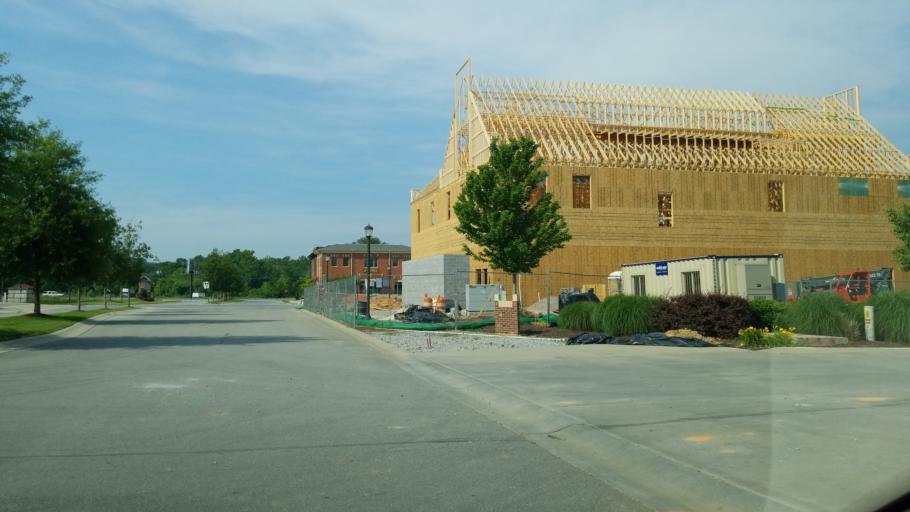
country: US
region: Tennessee
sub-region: Hamilton County
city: Collegedale
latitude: 35.0832
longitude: -85.0540
